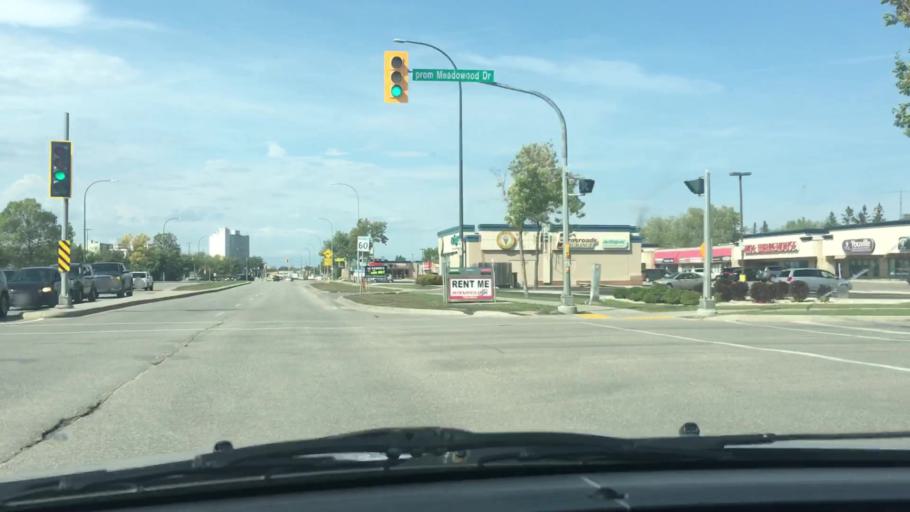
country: CA
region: Manitoba
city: Winnipeg
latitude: 49.8277
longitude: -97.1045
